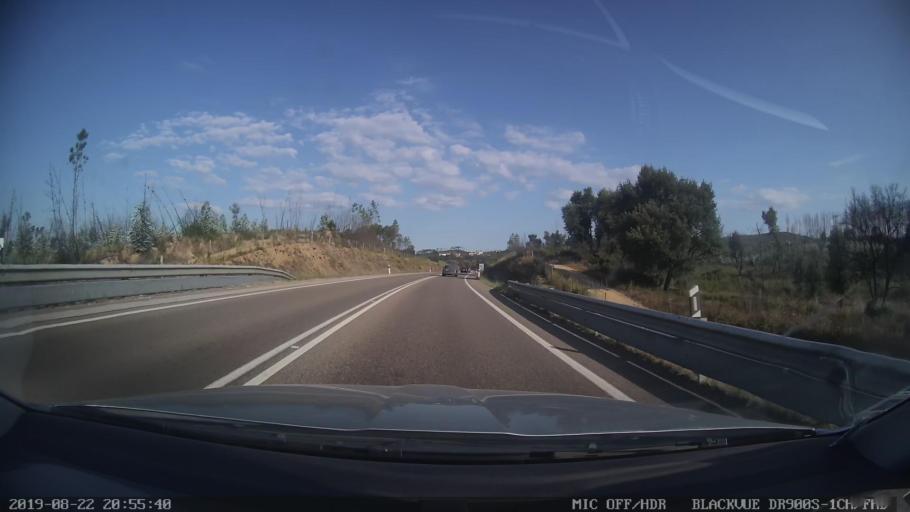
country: PT
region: Castelo Branco
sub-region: Serta
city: Serta
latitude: 39.7820
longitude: -8.0379
